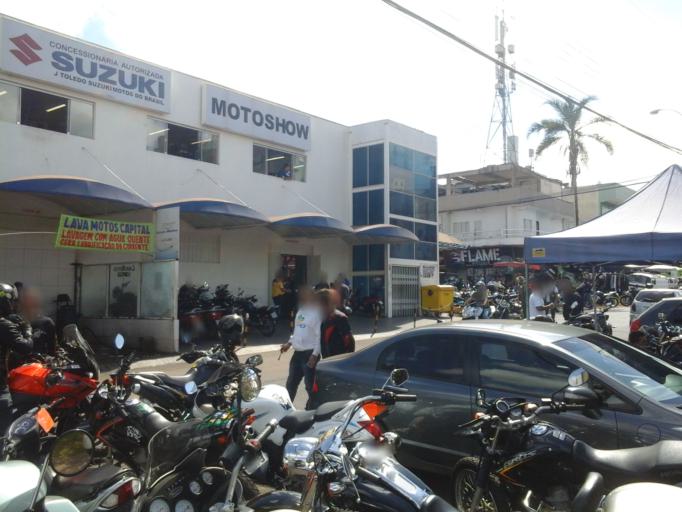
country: BR
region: Federal District
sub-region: Brasilia
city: Brasilia
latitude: -15.7890
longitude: -47.9184
